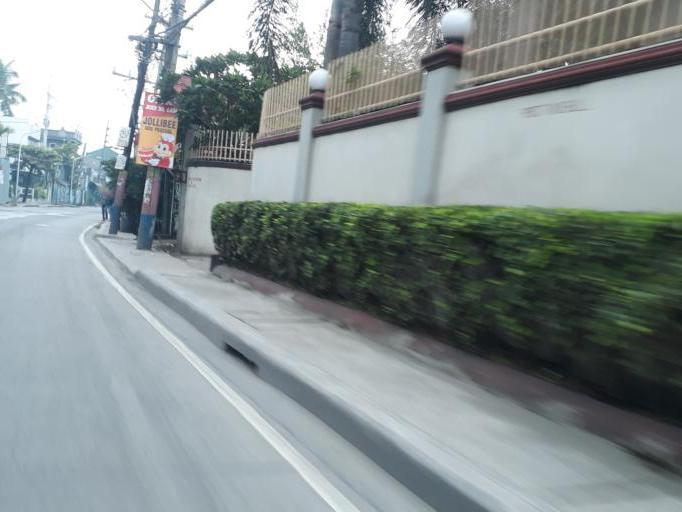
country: PH
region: Metro Manila
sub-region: Caloocan City
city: Niugan
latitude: 14.6722
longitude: 120.9637
